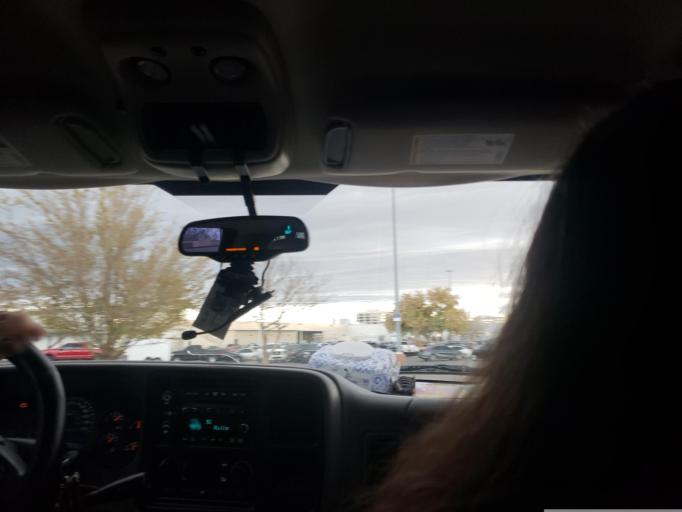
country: US
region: New Mexico
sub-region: Bernalillo County
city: Albuquerque
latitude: 35.1079
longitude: -106.5728
